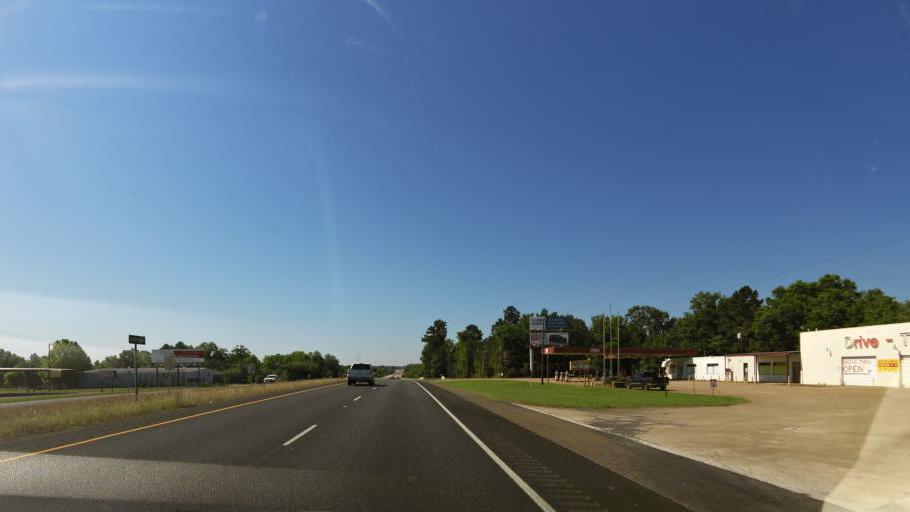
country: US
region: Texas
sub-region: Angelina County
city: Redland
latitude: 31.4662
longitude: -94.7266
